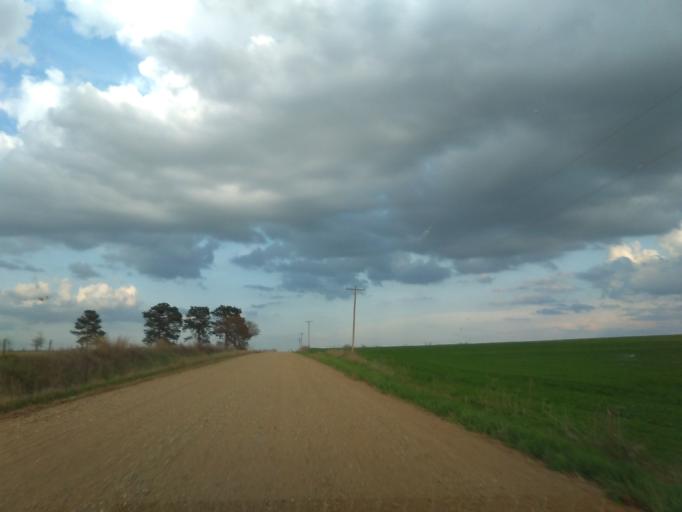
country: US
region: Nebraska
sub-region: Webster County
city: Red Cloud
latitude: 40.1762
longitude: -98.4380
